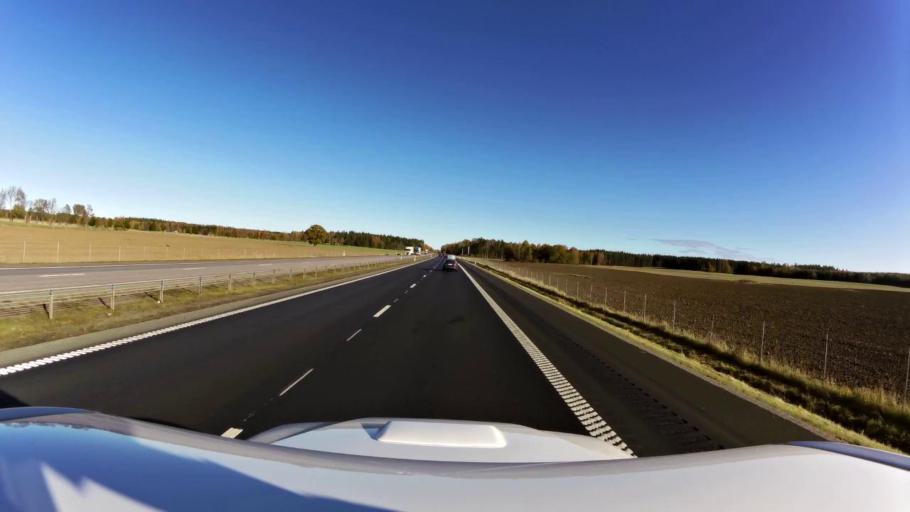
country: SE
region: OEstergoetland
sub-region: Linkopings Kommun
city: Malmslatt
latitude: 58.4143
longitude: 15.4713
